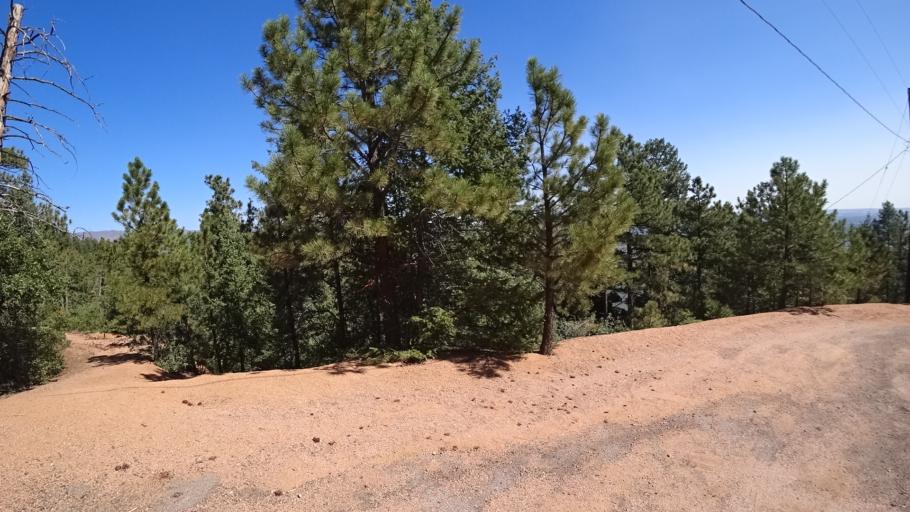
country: US
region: Colorado
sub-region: El Paso County
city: Manitou Springs
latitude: 38.8102
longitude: -104.8817
